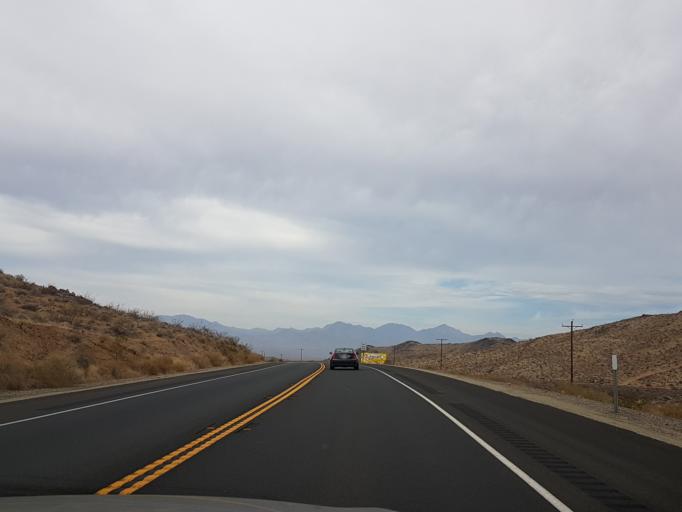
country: US
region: California
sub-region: Kern County
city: Ridgecrest
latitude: 35.5440
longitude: -117.6911
